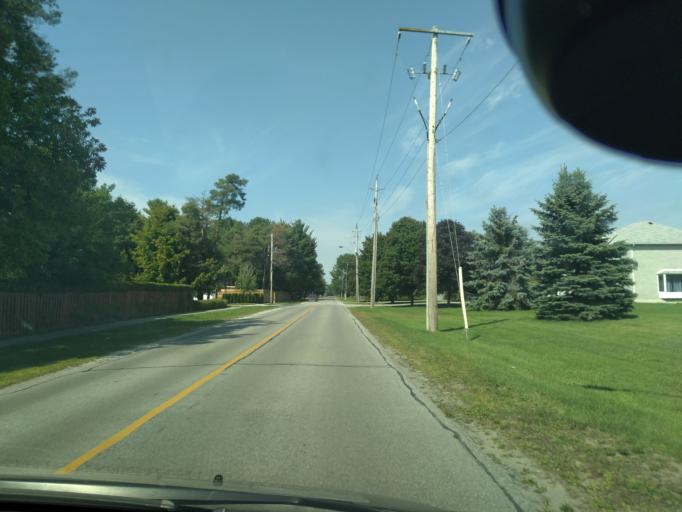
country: CA
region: Ontario
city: Newmarket
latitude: 44.1121
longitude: -79.5040
